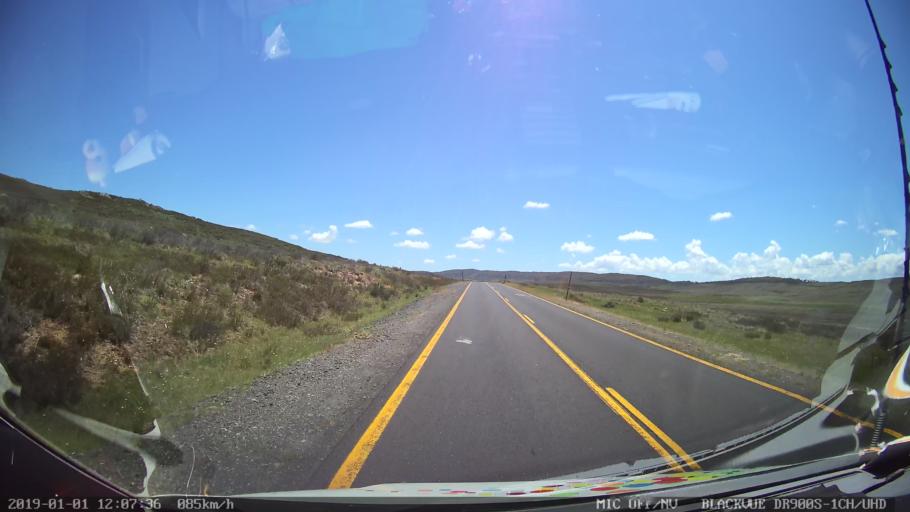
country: AU
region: New South Wales
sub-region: Tumut Shire
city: Tumut
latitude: -35.8309
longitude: 148.4905
